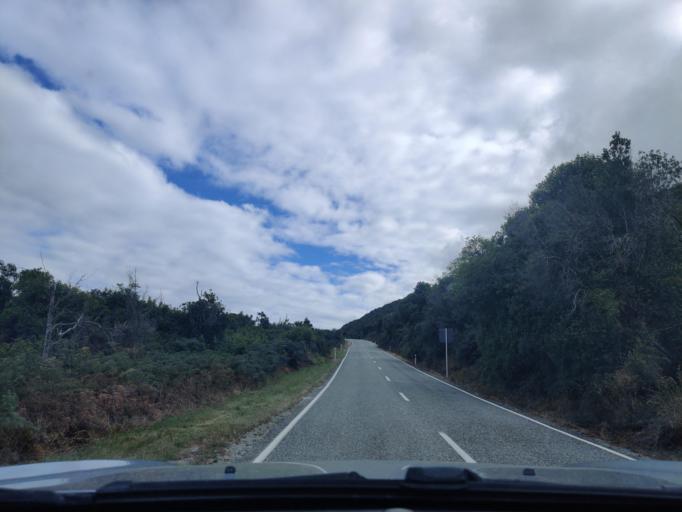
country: NZ
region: Otago
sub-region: Queenstown-Lakes District
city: Queenstown
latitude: -45.0750
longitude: 168.4655
